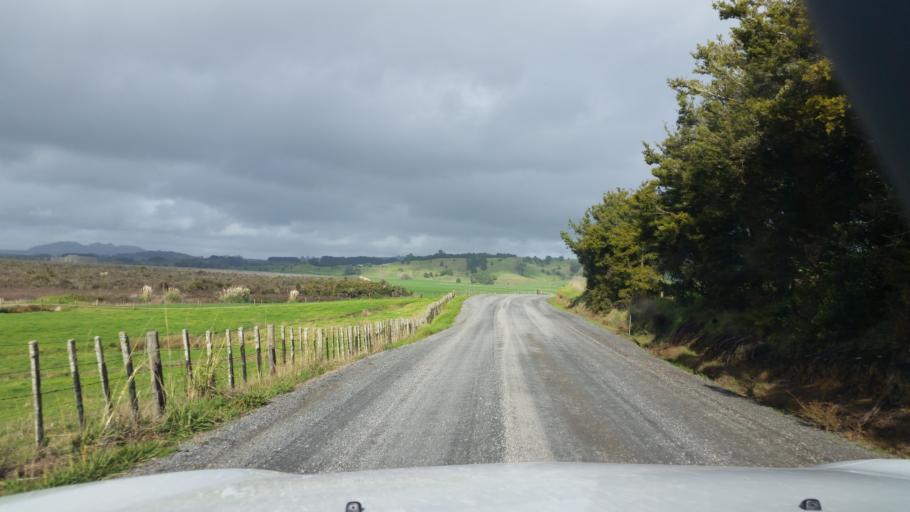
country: NZ
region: Northland
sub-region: Whangarei
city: Maungatapere
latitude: -35.5958
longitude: 174.1637
